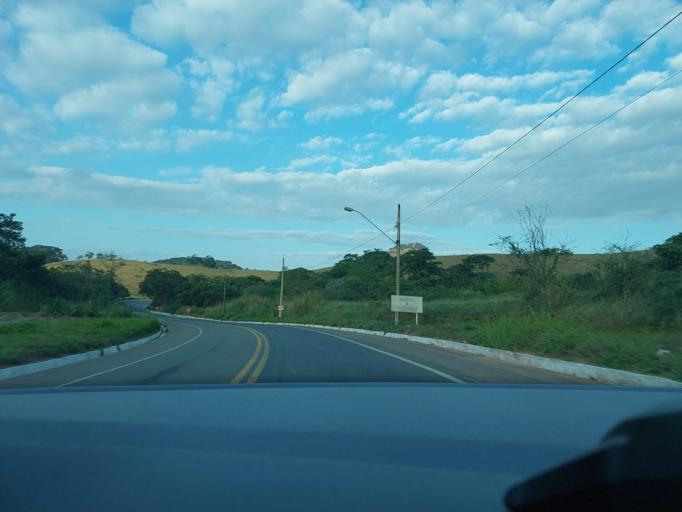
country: BR
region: Minas Gerais
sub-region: Muriae
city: Muriae
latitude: -21.1267
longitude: -42.3326
